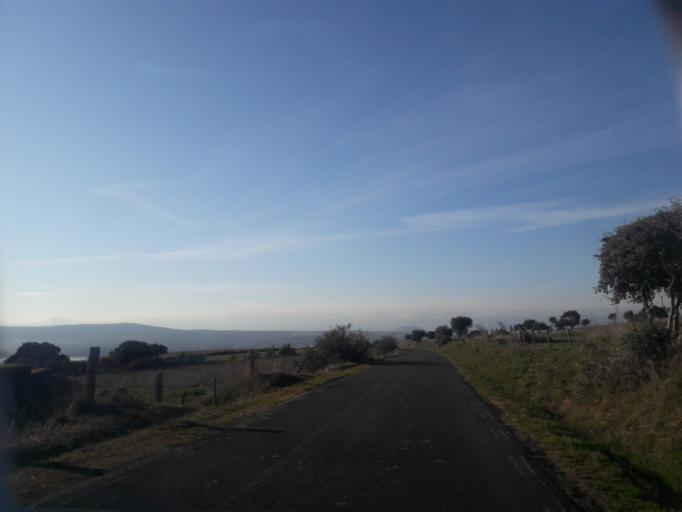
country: ES
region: Castille and Leon
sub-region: Provincia de Salamanca
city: Salvatierra de Tormes
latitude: 40.6062
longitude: -5.6013
